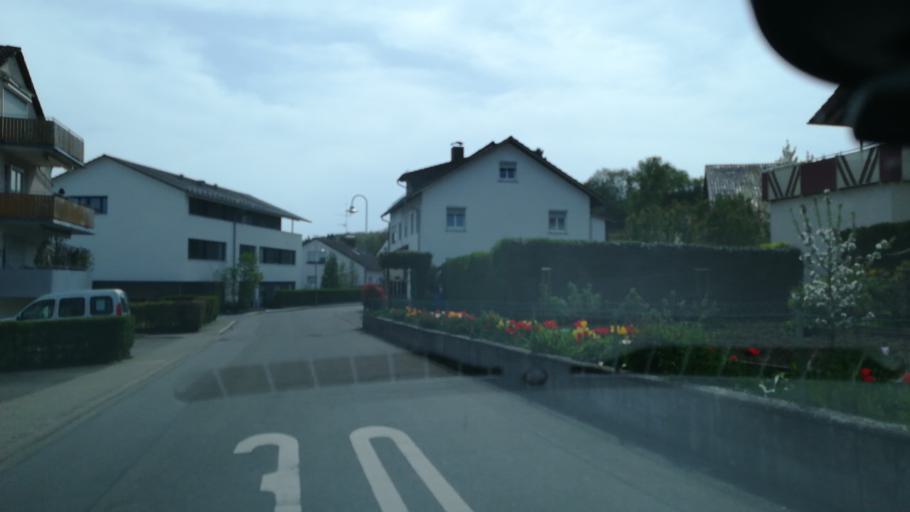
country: DE
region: Baden-Wuerttemberg
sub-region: Freiburg Region
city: Allensbach
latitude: 47.7346
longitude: 9.1136
